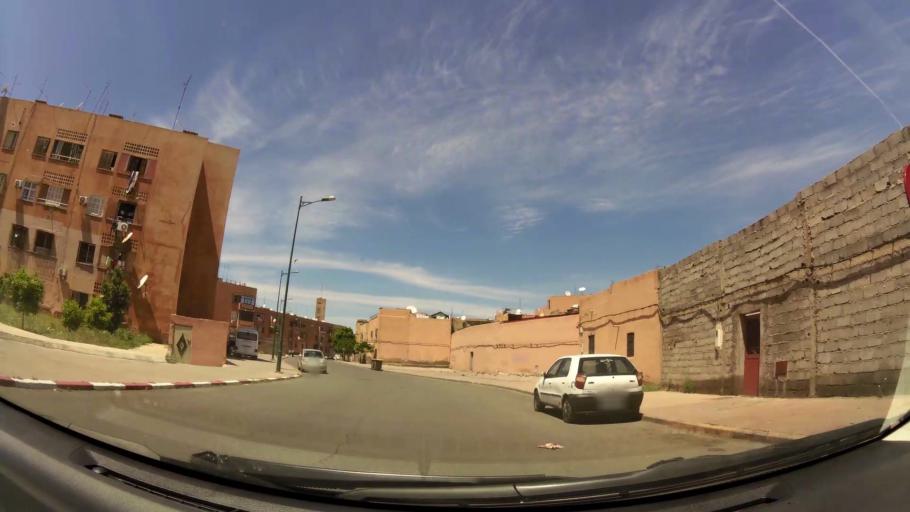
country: MA
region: Marrakech-Tensift-Al Haouz
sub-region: Marrakech
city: Marrakesh
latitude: 31.6312
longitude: -8.0013
